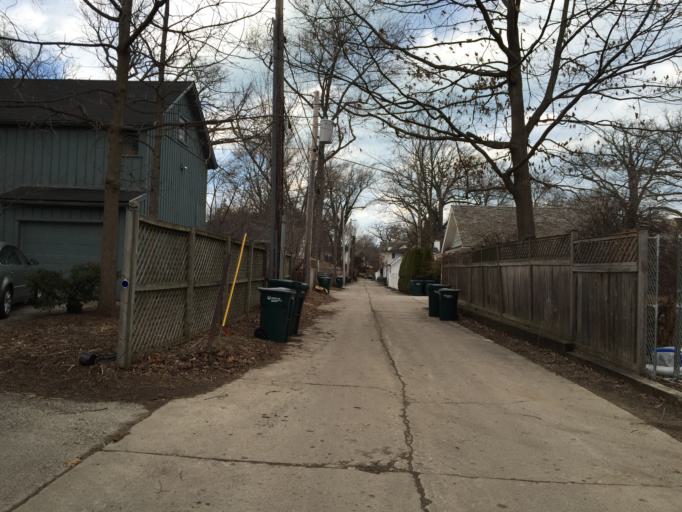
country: US
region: Illinois
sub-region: Cook County
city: Kenilworth
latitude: 42.0770
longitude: -87.7001
